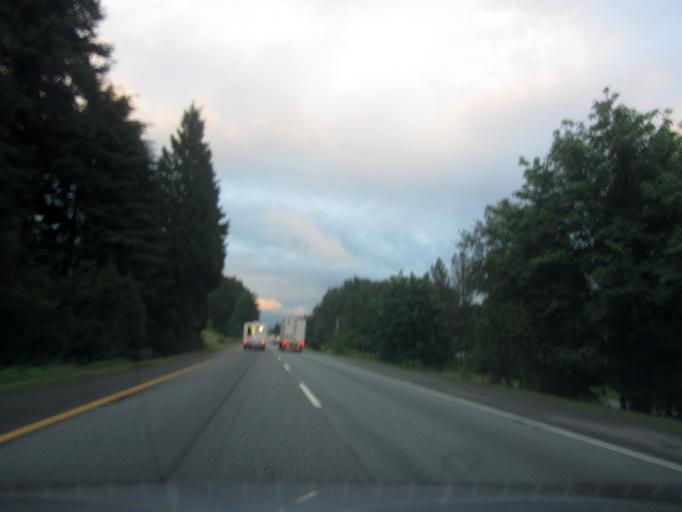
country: CA
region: British Columbia
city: Aldergrove
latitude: 49.0953
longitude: -122.4775
